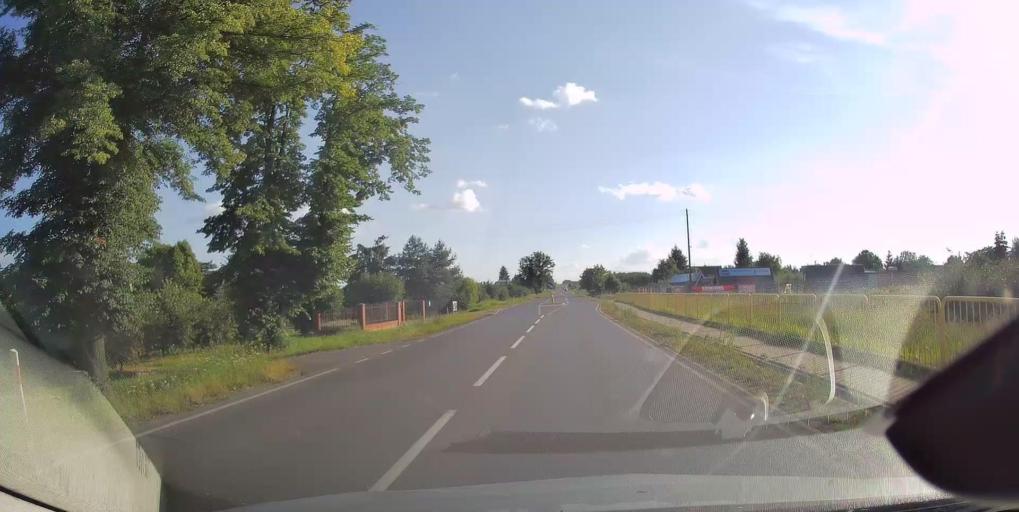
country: PL
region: Masovian Voivodeship
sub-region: Powiat grojecki
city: Grojec
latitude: 51.8480
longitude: 20.8380
